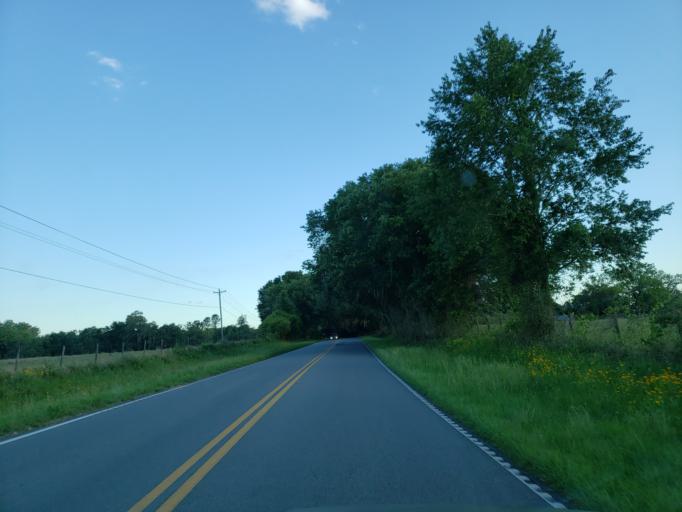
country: US
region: Georgia
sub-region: Lowndes County
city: Valdosta
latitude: 30.7170
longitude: -83.2429
